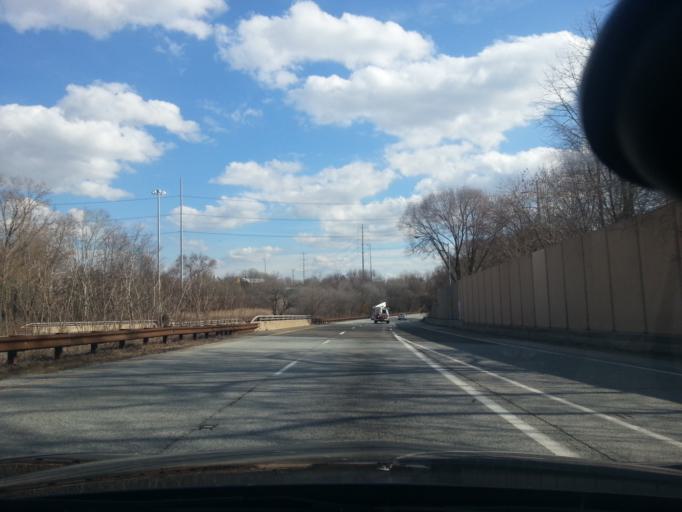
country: US
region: Pennsylvania
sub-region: Delaware County
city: Woodlyn
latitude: 39.8697
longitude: -75.3466
